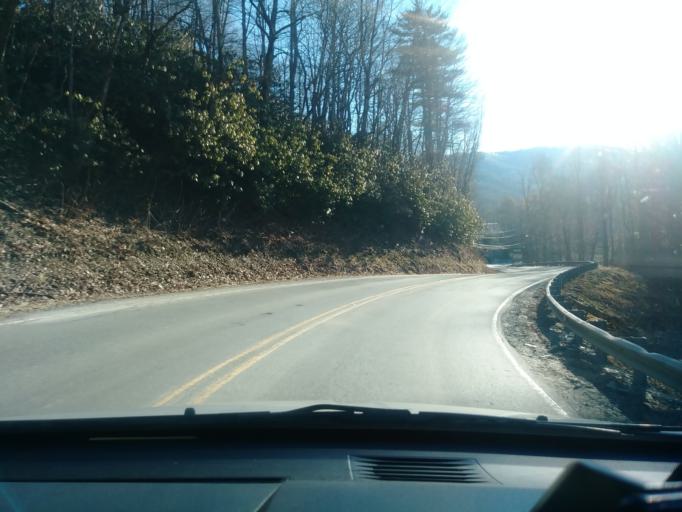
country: US
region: North Carolina
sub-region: Avery County
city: Banner Elk
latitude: 36.1601
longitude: -81.8846
